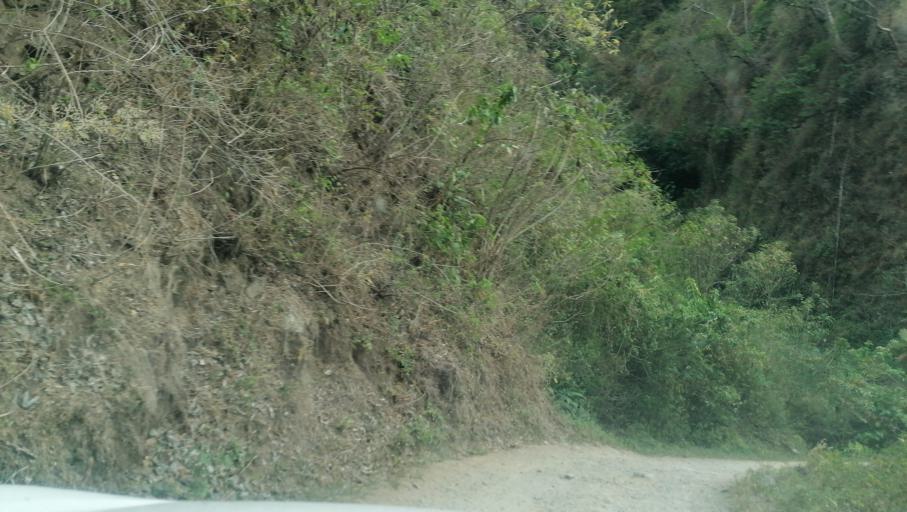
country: MX
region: Chiapas
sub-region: Cacahoatan
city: Benito Juarez
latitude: 15.1605
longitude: -92.1771
